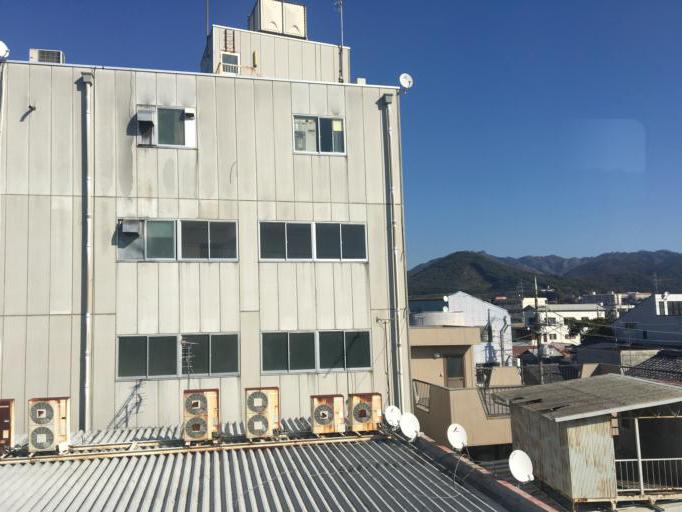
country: JP
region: Gunma
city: Kiryu
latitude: 36.4083
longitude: 139.3396
